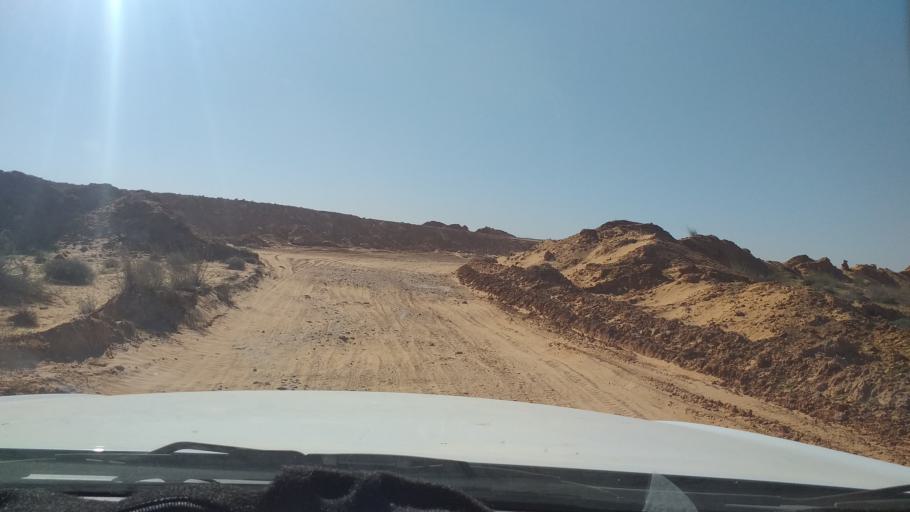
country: TN
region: Madanin
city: Medenine
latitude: 33.2675
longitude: 10.5833
